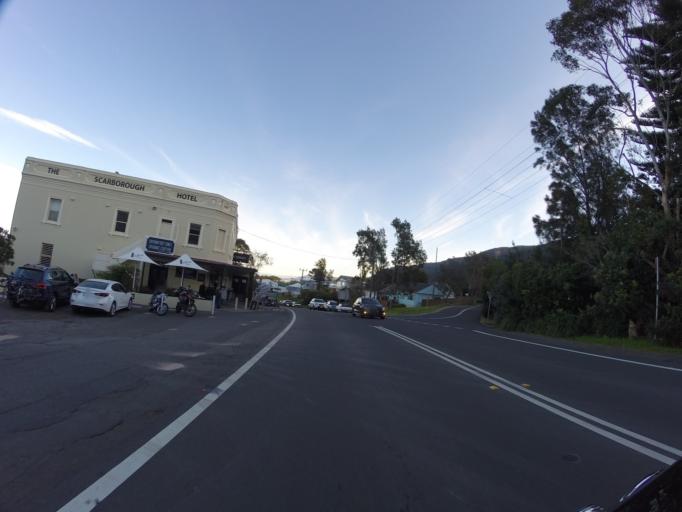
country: AU
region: New South Wales
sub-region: Wollongong
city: Bulli
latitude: -34.2692
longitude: 150.9615
